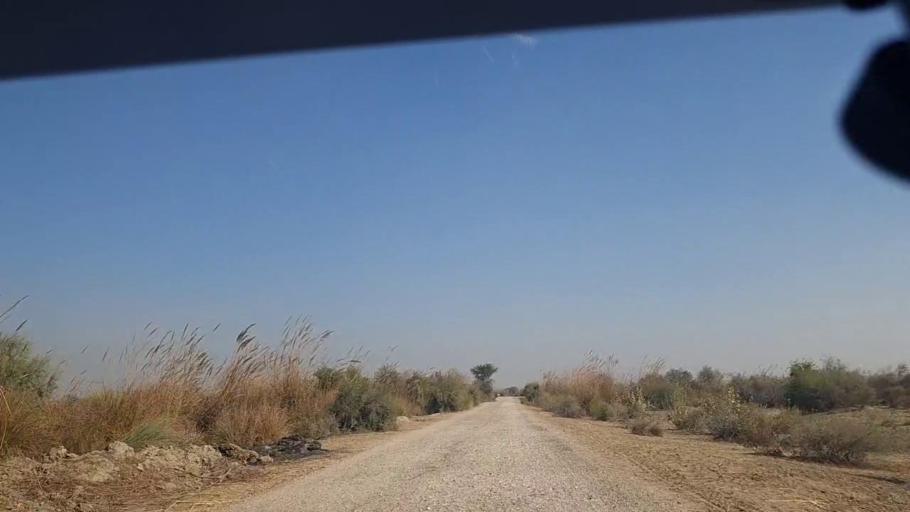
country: PK
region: Sindh
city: Khanpur
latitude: 27.5640
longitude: 69.3115
